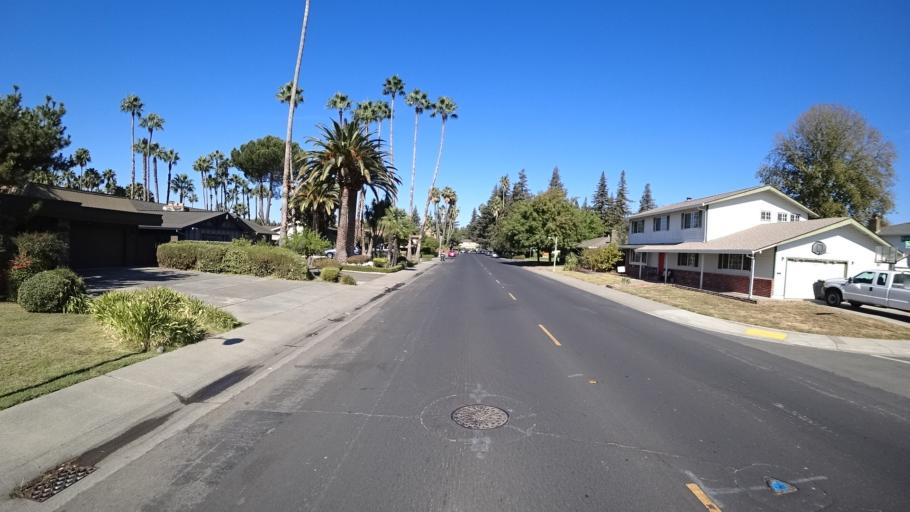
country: US
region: California
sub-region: Yolo County
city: West Sacramento
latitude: 38.5107
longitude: -121.5322
